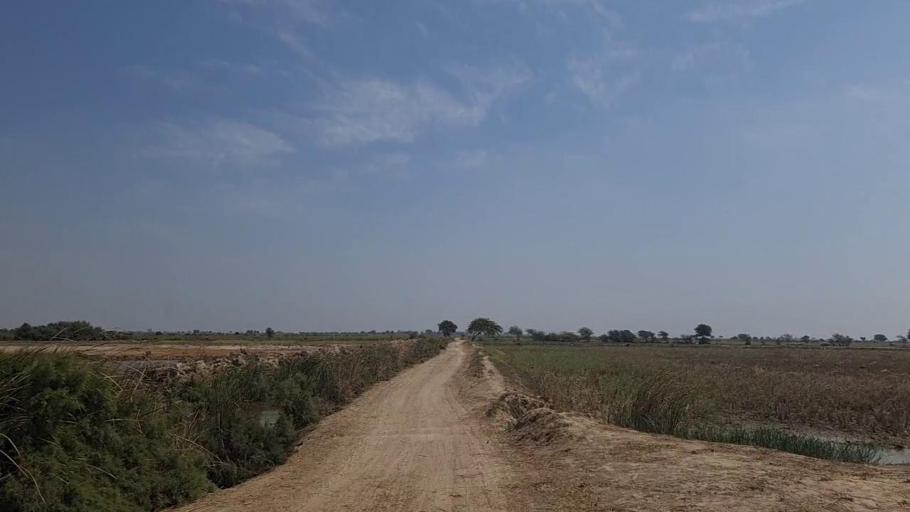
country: PK
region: Sindh
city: Mirpur Batoro
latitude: 24.5844
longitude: 68.2977
